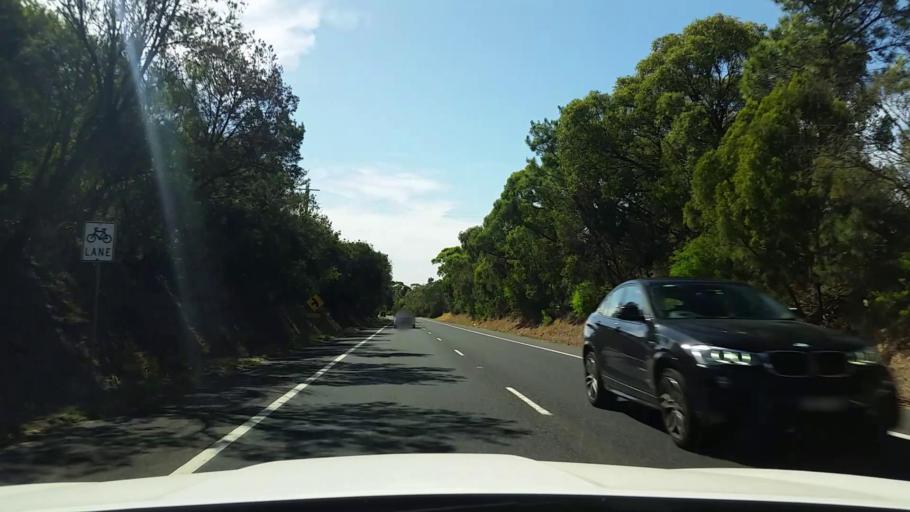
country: AU
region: Victoria
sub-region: Mornington Peninsula
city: Mount Martha
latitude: -38.2815
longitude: 145.0323
